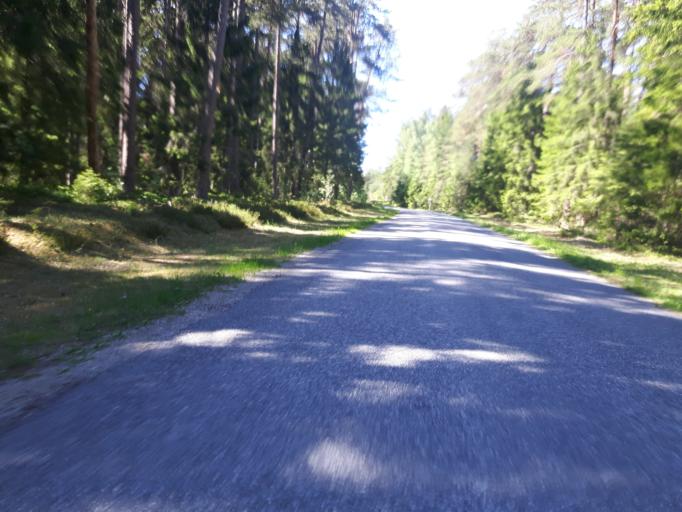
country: EE
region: Laeaene-Virumaa
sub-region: Haljala vald
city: Haljala
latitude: 59.5748
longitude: 26.2787
